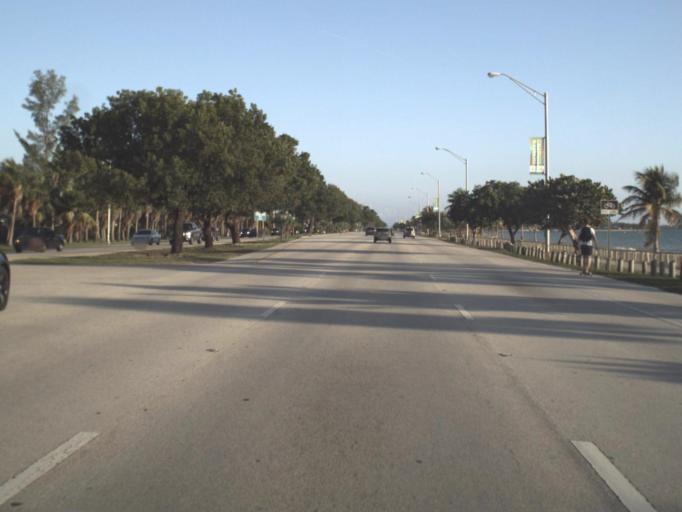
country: US
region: Florida
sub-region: Miami-Dade County
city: Miami
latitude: 25.7446
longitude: -80.1747
